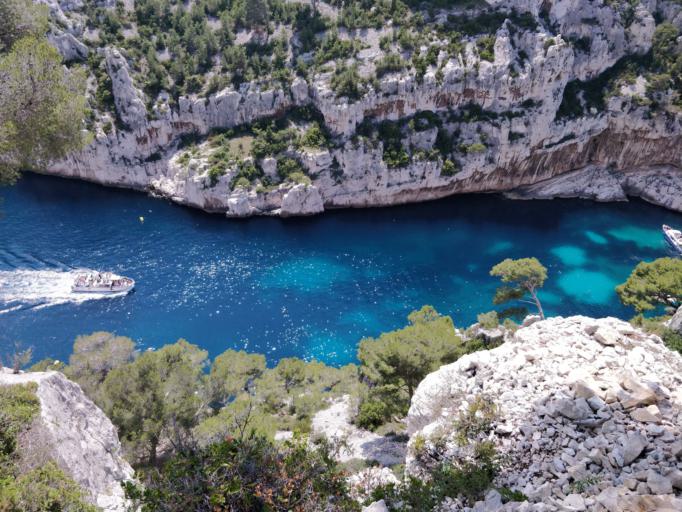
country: FR
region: Provence-Alpes-Cote d'Azur
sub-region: Departement des Bouches-du-Rhone
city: Cassis
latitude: 43.2015
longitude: 5.5028
